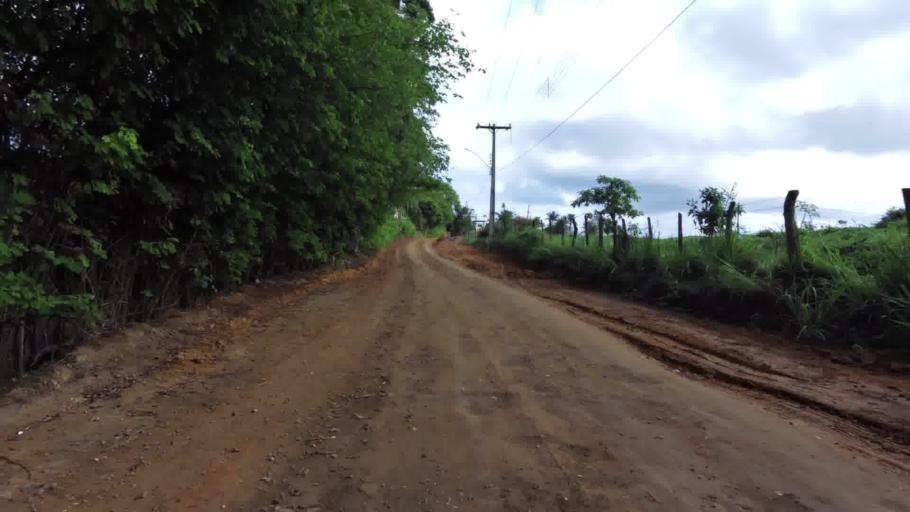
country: BR
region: Espirito Santo
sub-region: Piuma
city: Piuma
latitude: -20.8098
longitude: -40.6640
